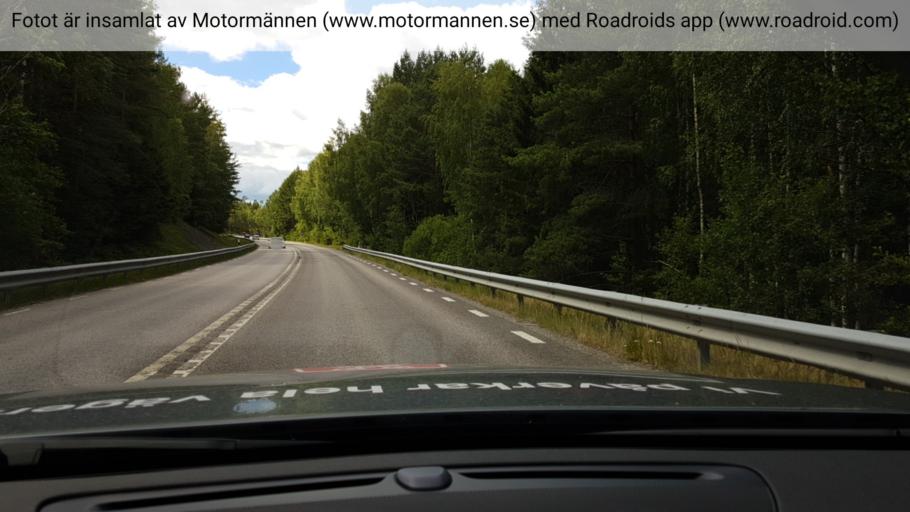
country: SE
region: Stockholm
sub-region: Osterakers Kommun
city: Akersberga
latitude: 59.4283
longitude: 18.2347
